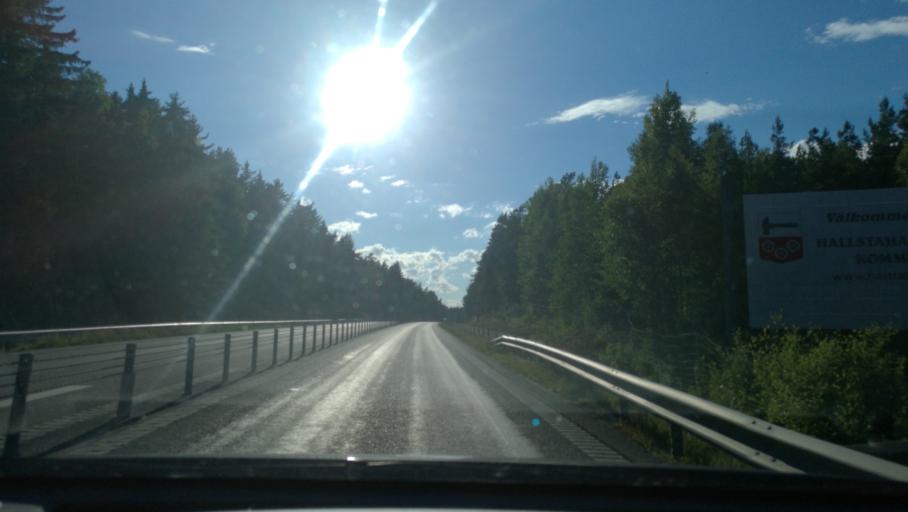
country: SE
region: Vaestmanland
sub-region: Hallstahammars Kommun
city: Kolback
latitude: 59.5791
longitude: 16.3070
